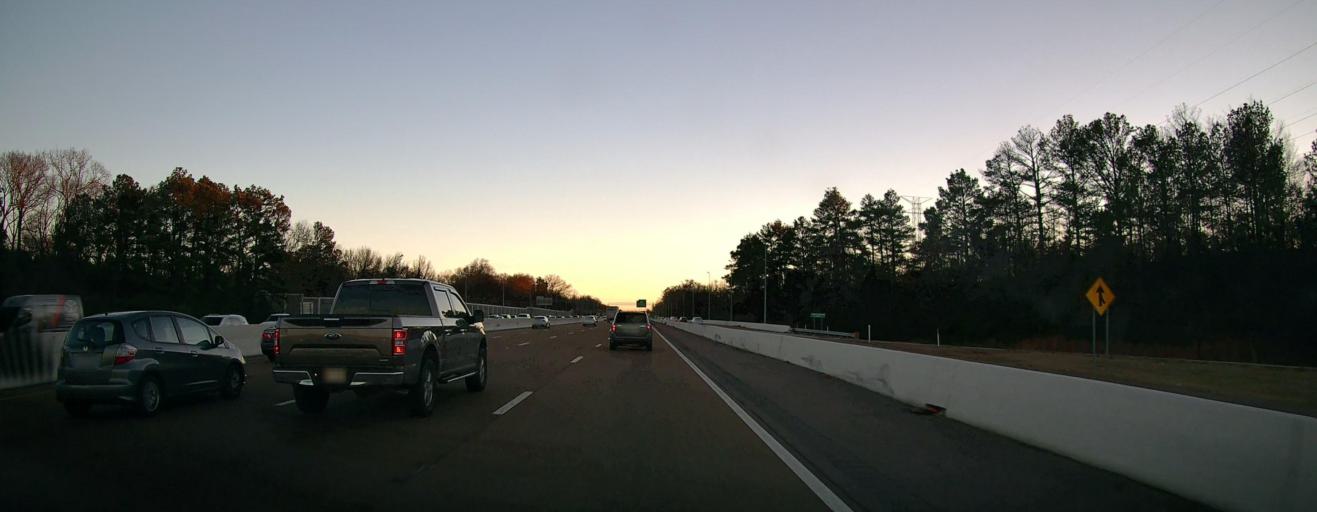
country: US
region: Tennessee
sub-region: Shelby County
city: Germantown
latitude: 35.1296
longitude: -89.8684
